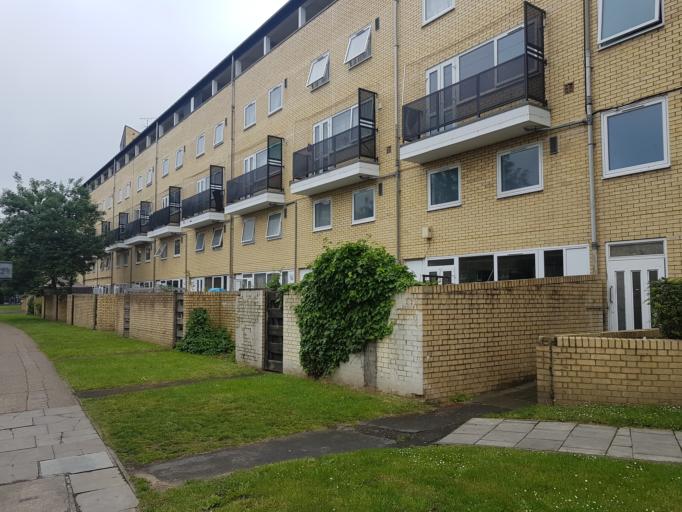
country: GB
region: England
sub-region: Greater London
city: Camberwell
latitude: 51.4775
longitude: -0.0700
